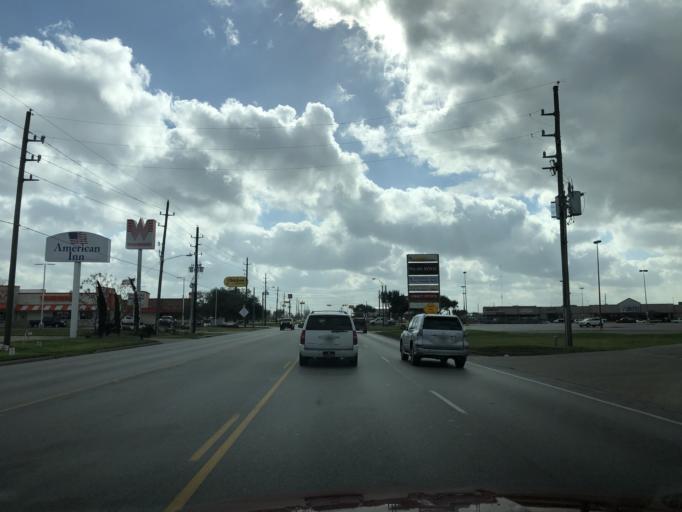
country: US
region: Texas
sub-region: Austin County
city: Sealy
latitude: 29.7624
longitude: -96.1521
